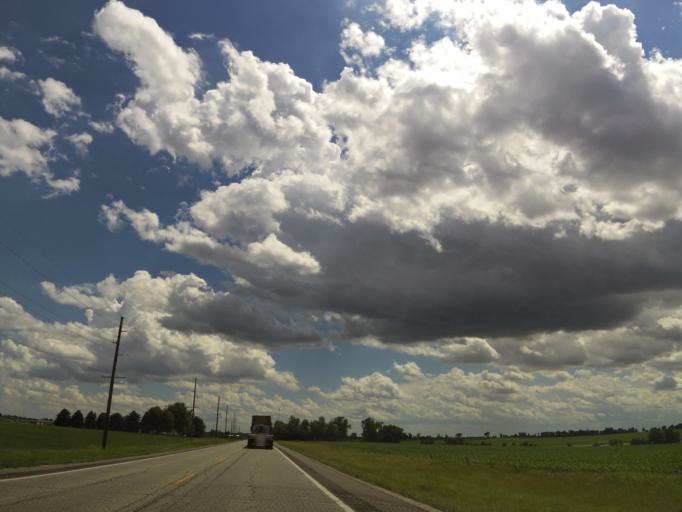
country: US
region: Iowa
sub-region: Benton County
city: Urbana
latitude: 42.2526
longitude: -91.8908
